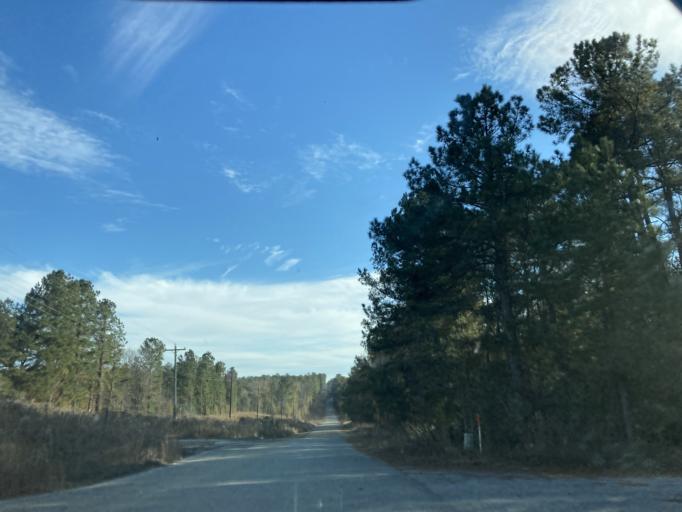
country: US
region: Georgia
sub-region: Jones County
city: Gray
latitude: 32.9266
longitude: -83.4987
